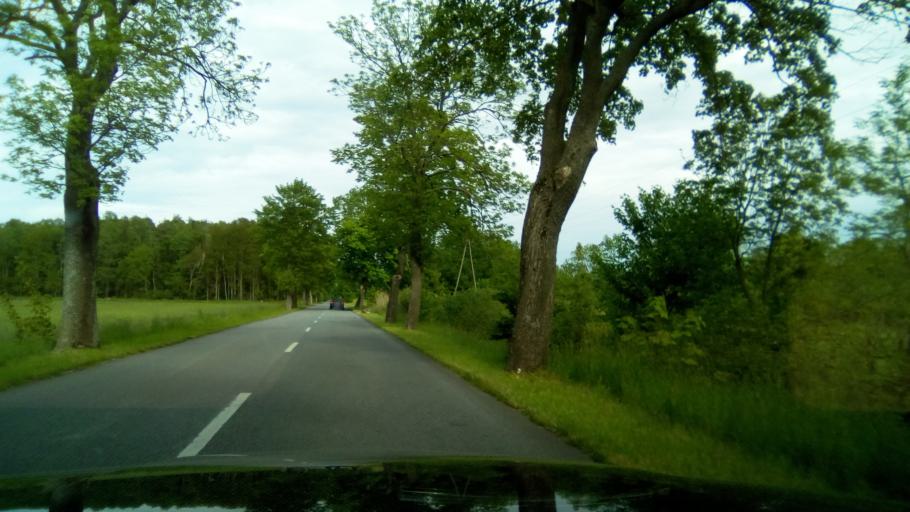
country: PL
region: Pomeranian Voivodeship
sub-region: Powiat pucki
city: Wierzchucino
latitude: 54.7947
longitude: 18.0342
